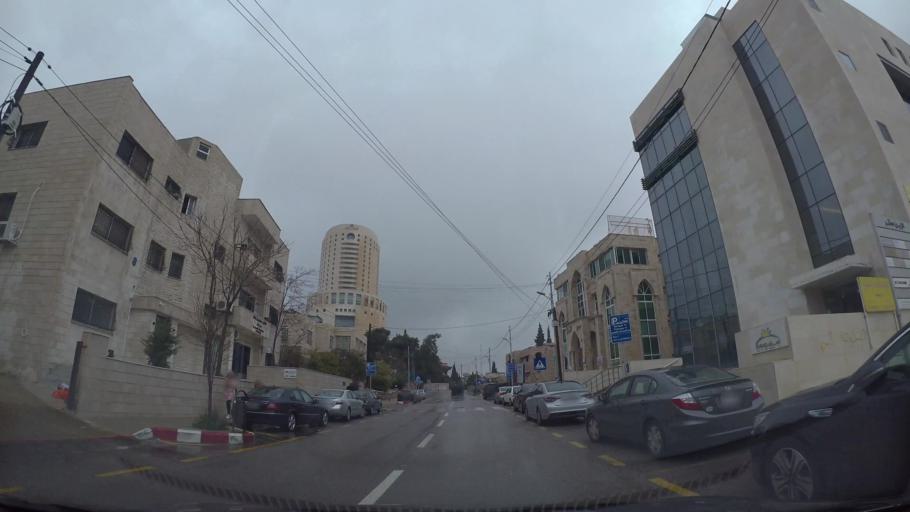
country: JO
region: Amman
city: Amman
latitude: 31.9508
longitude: 35.9080
